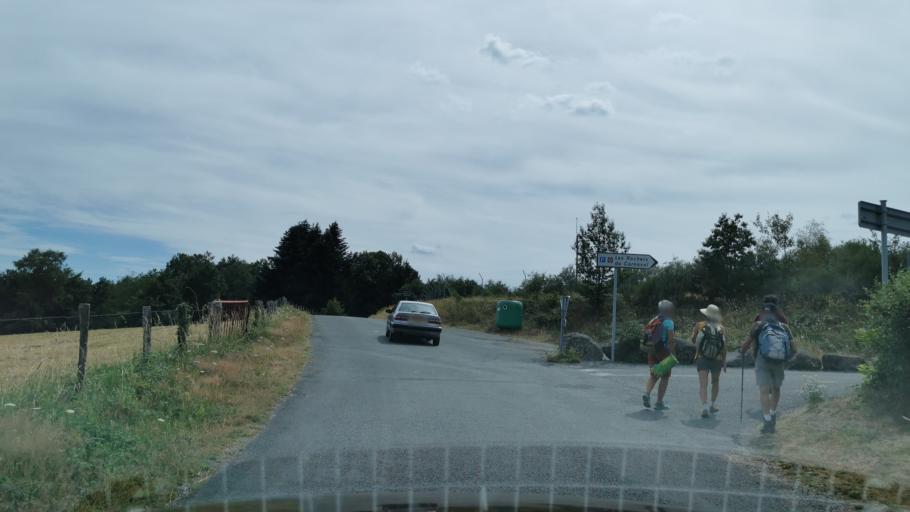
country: FR
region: Bourgogne
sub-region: Departement de Saone-et-Loire
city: Etang-sur-Arroux
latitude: 46.8065
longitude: 4.2602
